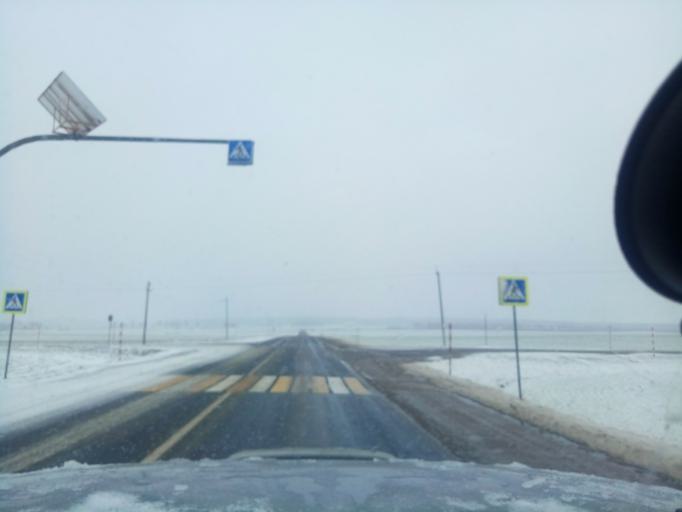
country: BY
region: Minsk
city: Nyasvizh
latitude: 53.2029
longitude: 26.6767
